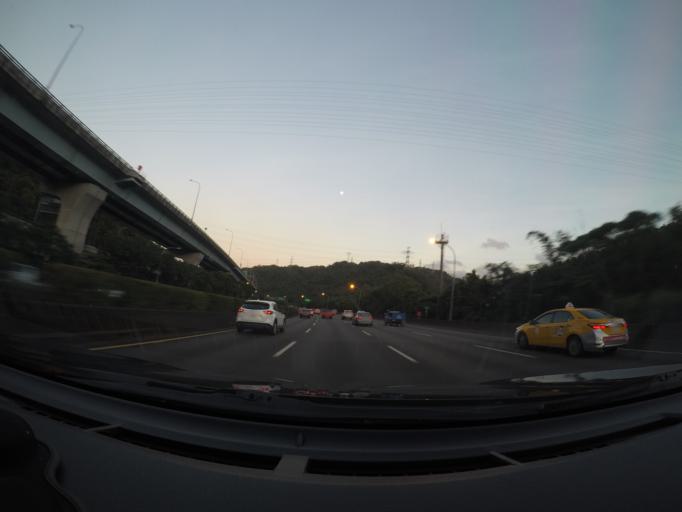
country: TW
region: Taipei
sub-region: Taipei
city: Banqiao
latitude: 25.0561
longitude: 121.4025
